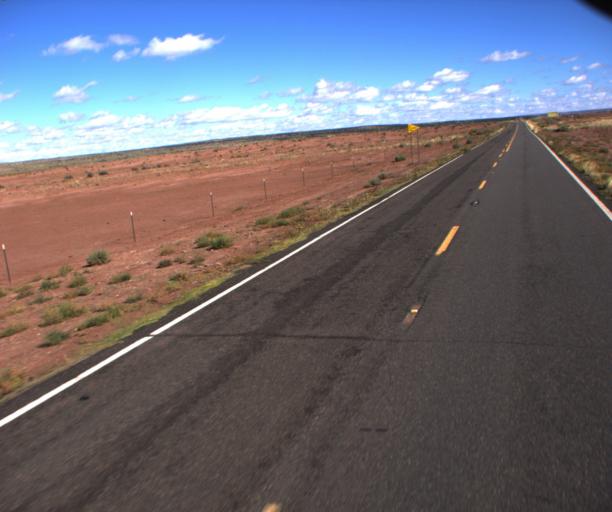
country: US
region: Arizona
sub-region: Apache County
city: Saint Johns
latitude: 34.6937
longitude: -109.2750
